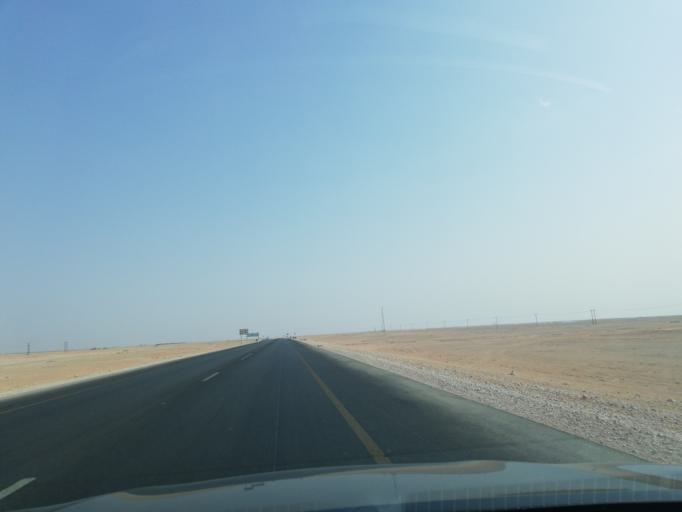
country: OM
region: Zufar
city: Salalah
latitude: 17.9026
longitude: 54.0095
